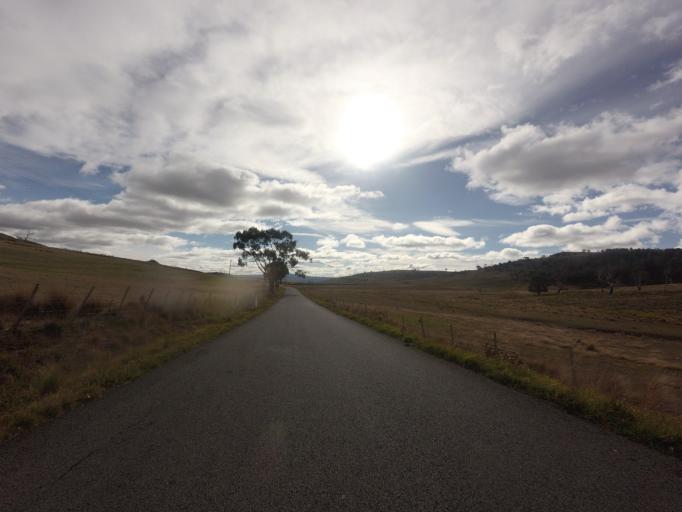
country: AU
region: Tasmania
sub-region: Brighton
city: Bridgewater
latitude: -42.3742
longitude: 147.3581
